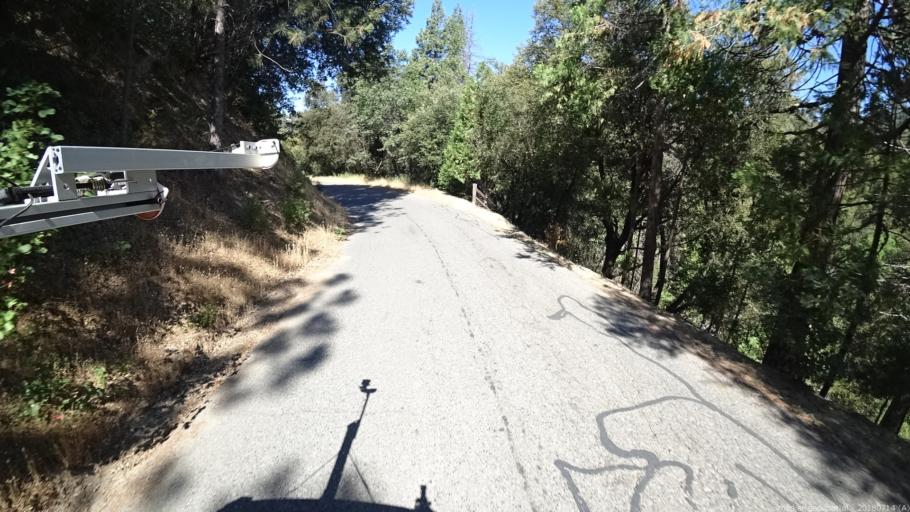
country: US
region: California
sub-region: Madera County
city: Oakhurst
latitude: 37.3720
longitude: -119.6249
